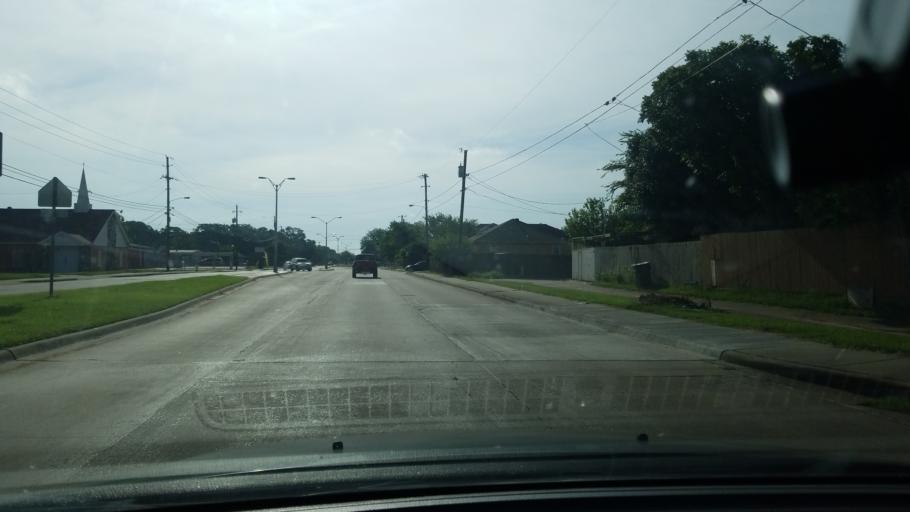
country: US
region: Texas
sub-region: Dallas County
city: Balch Springs
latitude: 32.7194
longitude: -96.6414
